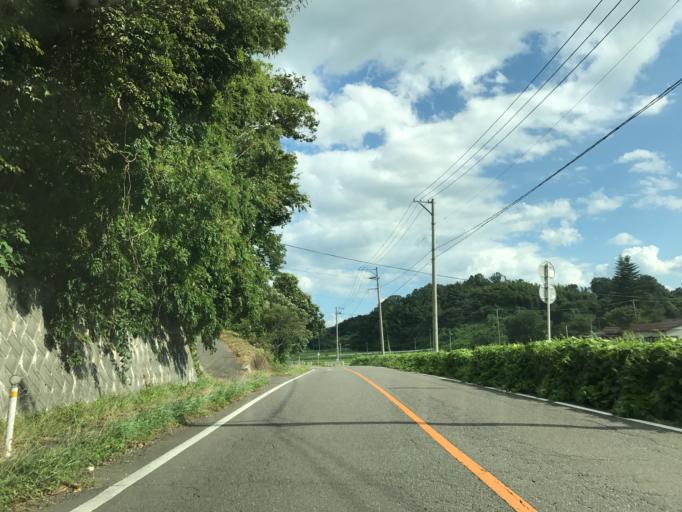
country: JP
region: Fukushima
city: Koriyama
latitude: 37.4076
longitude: 140.4345
